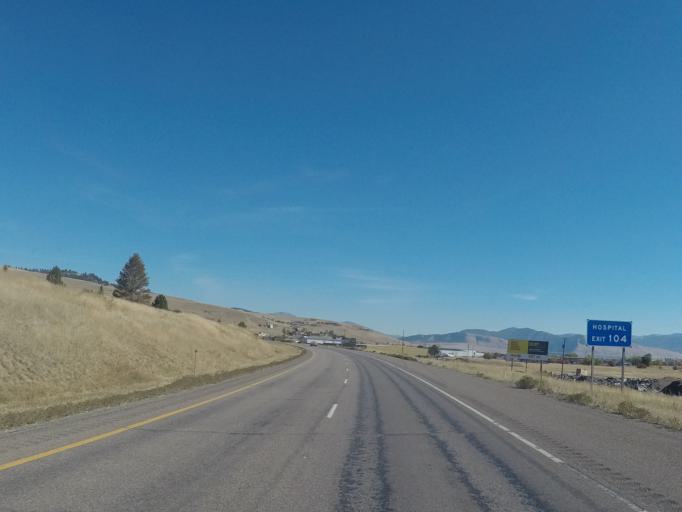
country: US
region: Montana
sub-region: Missoula County
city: Orchard Homes
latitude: 46.9389
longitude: -114.1089
